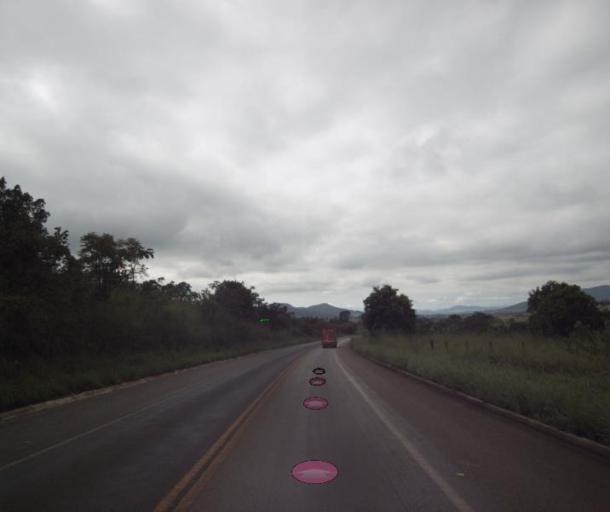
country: BR
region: Goias
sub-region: Barro Alto
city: Barro Alto
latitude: -14.9389
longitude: -48.9407
